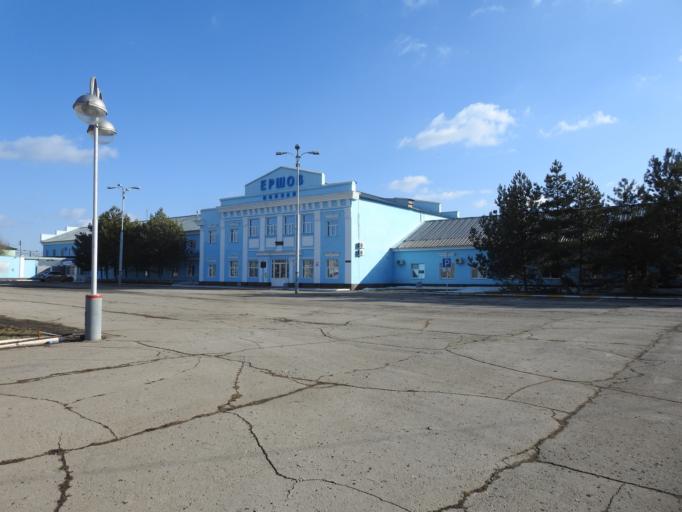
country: RU
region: Saratov
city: Yershov
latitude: 51.3487
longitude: 48.2765
